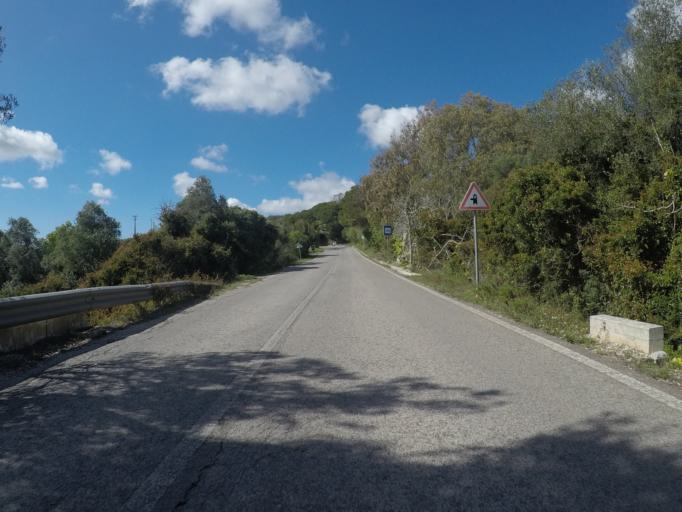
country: PT
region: Faro
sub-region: Vila do Bispo
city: Vila do Bispo
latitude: 37.0760
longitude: -8.8315
